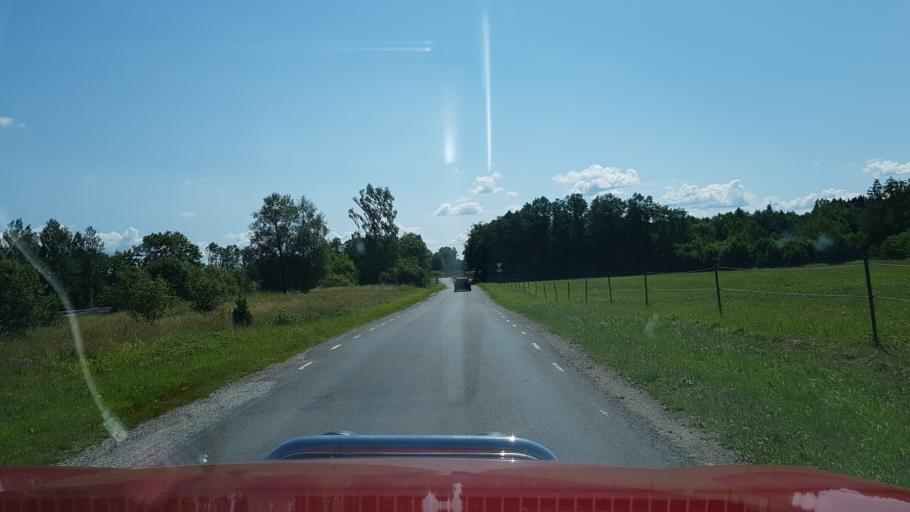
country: EE
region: Harju
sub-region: Saue linn
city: Saue
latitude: 59.1623
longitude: 24.5026
